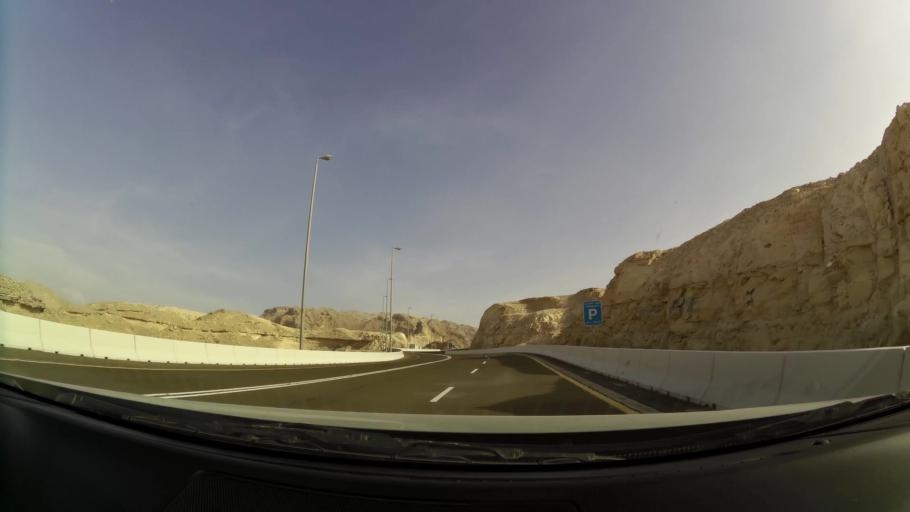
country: AE
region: Abu Dhabi
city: Al Ain
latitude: 24.1094
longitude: 55.7572
